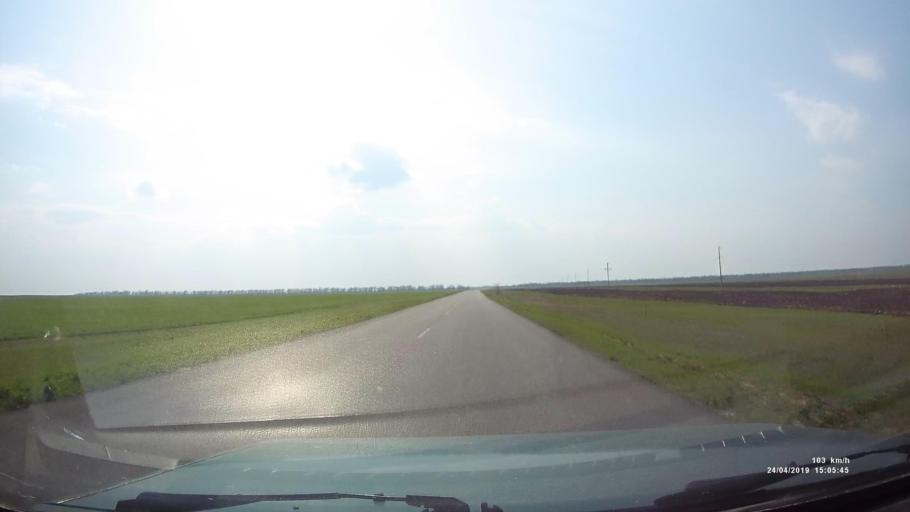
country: RU
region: Rostov
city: Remontnoye
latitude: 46.5596
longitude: 43.4420
